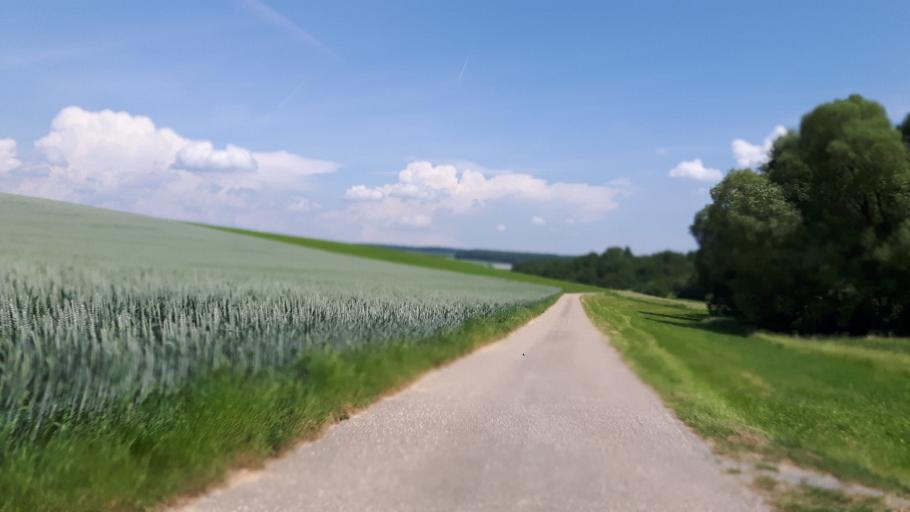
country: DE
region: Baden-Wuerttemberg
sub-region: Regierungsbezirk Stuttgart
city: Neuenstadt am Kocher
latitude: 49.2319
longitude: 9.3096
